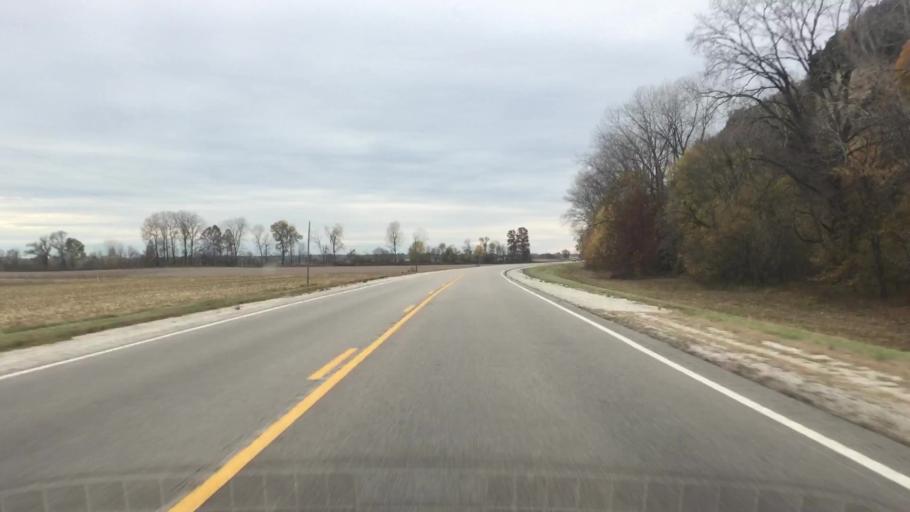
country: US
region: Missouri
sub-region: Callaway County
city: Holts Summit
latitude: 38.5838
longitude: -92.1138
